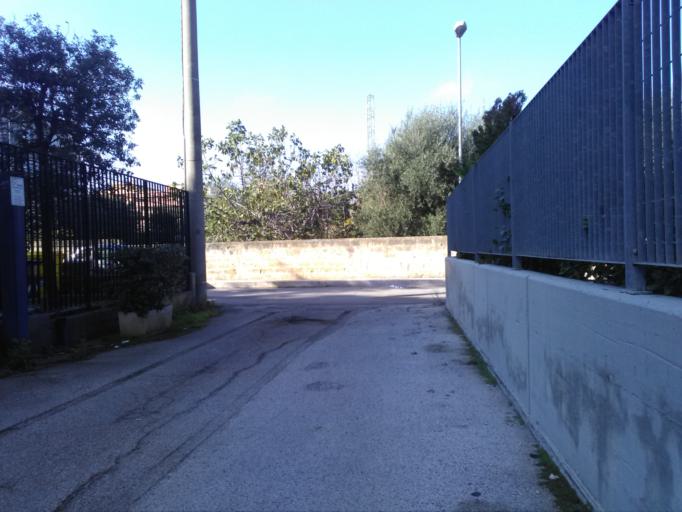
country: IT
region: Apulia
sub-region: Provincia di Bari
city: San Paolo
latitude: 41.1547
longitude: 16.7686
